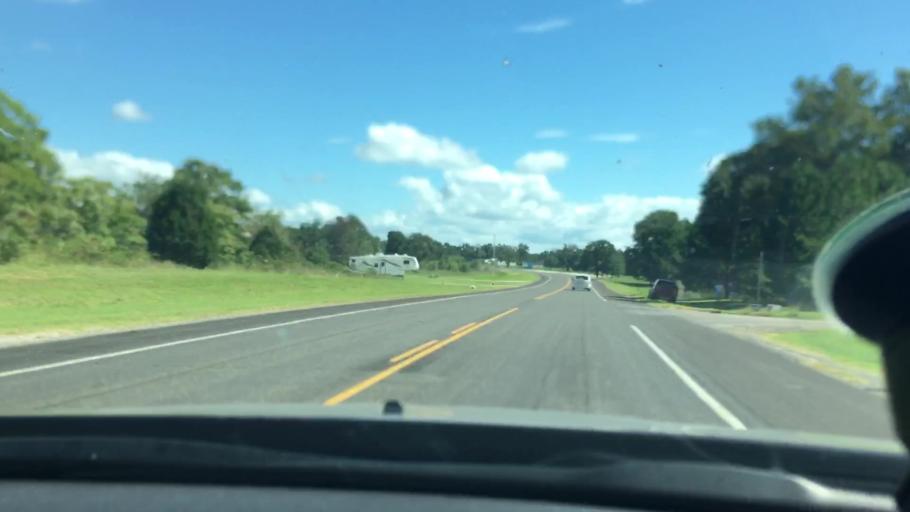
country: US
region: Oklahoma
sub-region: Sequoyah County
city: Vian
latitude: 35.5589
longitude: -94.9802
